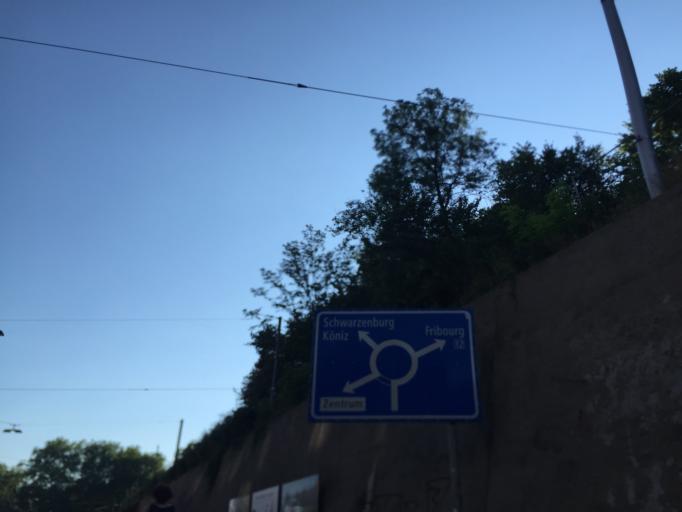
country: CH
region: Bern
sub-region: Bern-Mittelland District
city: Koniz
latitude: 46.9453
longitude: 7.4231
